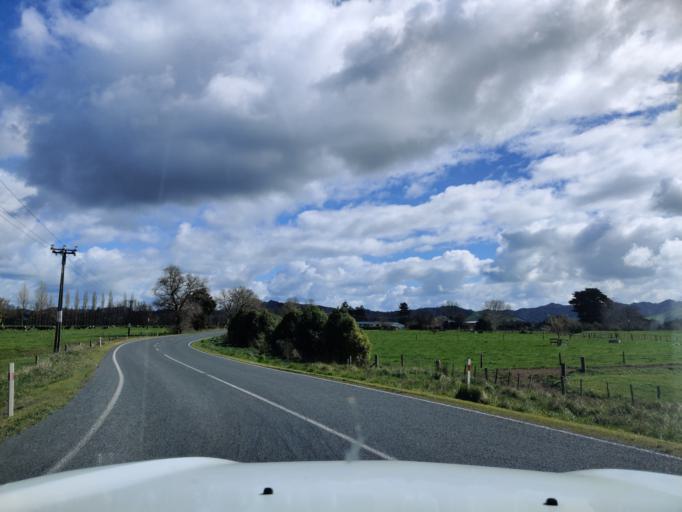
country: NZ
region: Waikato
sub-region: Waikato District
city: Ngaruawahia
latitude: -37.5681
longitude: 175.2630
